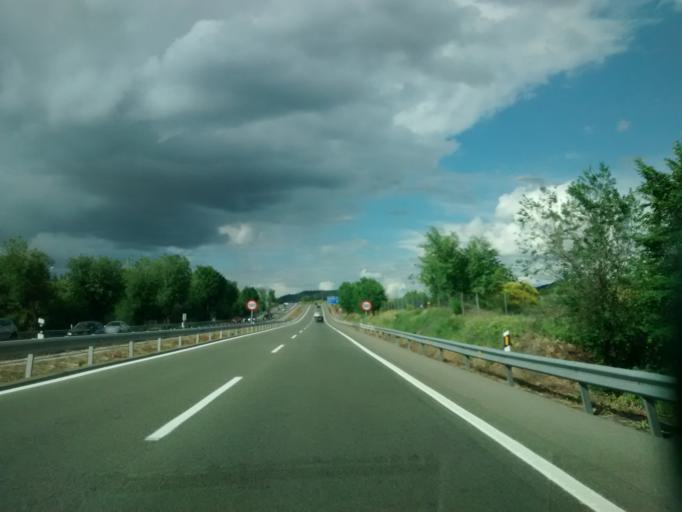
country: ES
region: Castille-La Mancha
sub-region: Provincia de Guadalajara
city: Guadalajara
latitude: 40.6332
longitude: -3.1459
